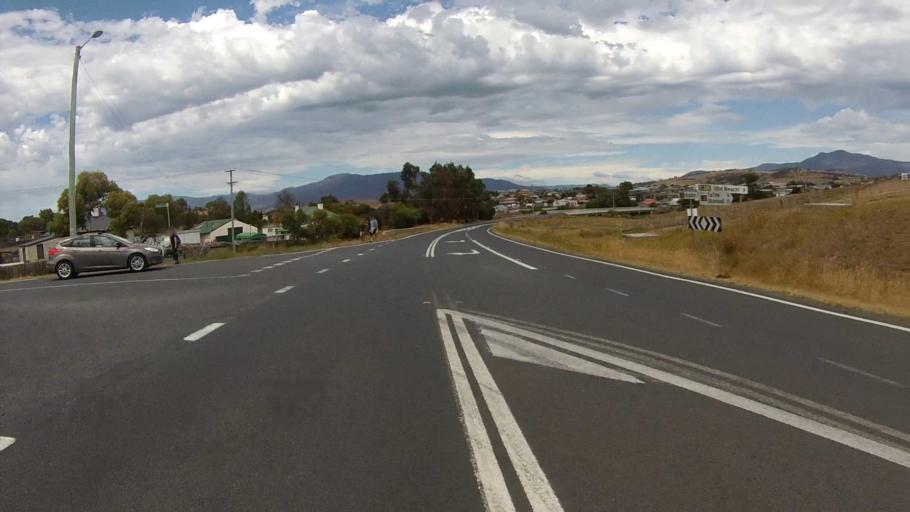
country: AU
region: Tasmania
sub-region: Brighton
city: Bridgewater
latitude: -42.7006
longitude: 147.2683
